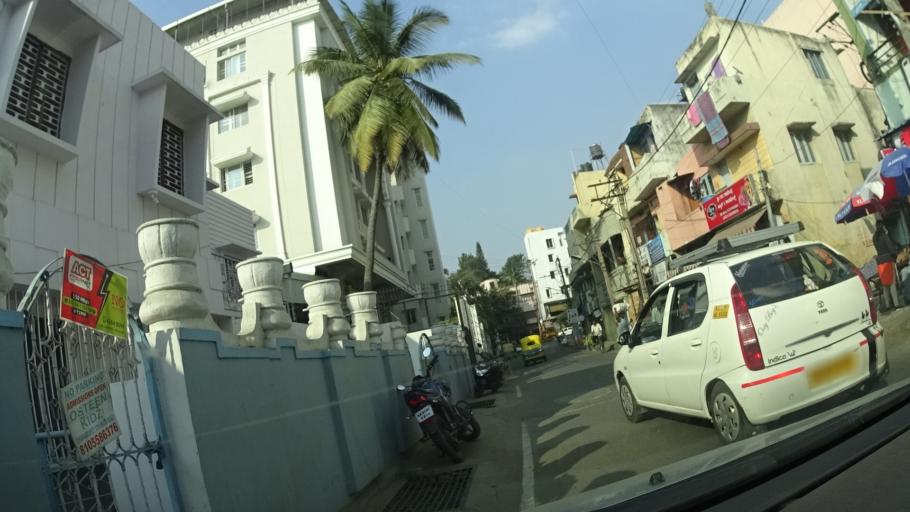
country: IN
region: Karnataka
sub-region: Bangalore Urban
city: Bangalore
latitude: 12.9542
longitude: 77.5653
